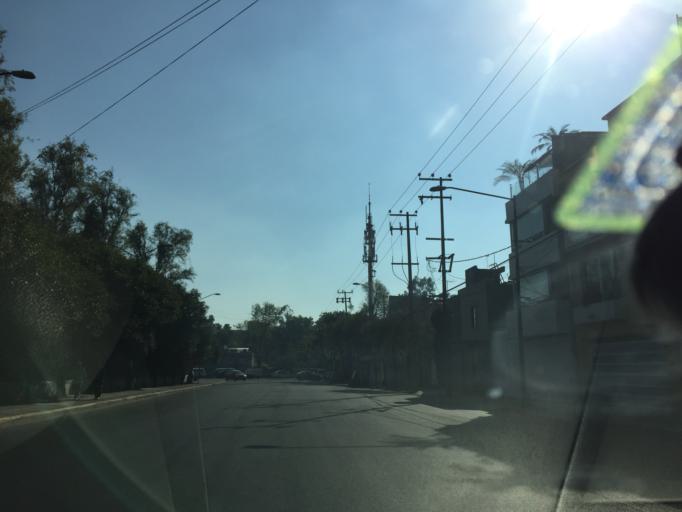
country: MX
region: Mexico
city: Vista Hermosa
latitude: 19.4967
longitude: -99.2078
